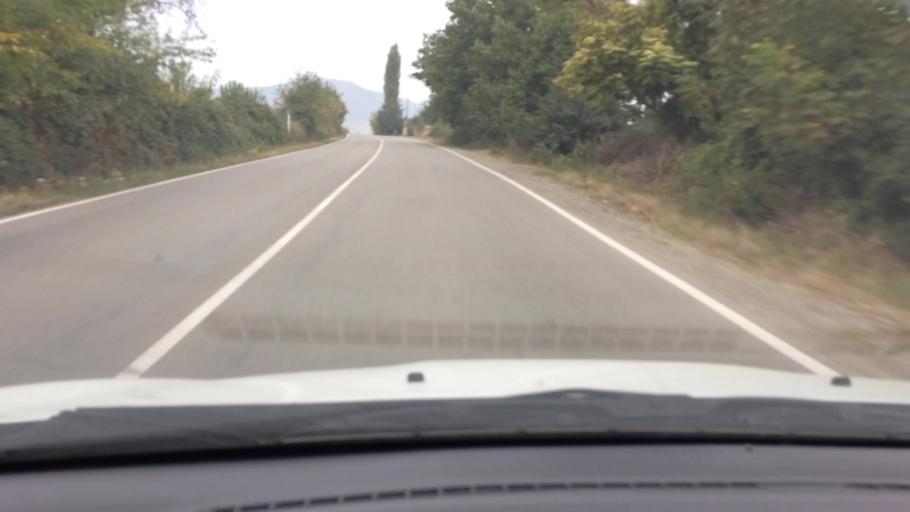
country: AM
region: Tavush
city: Bagratashen
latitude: 41.2351
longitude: 44.8093
